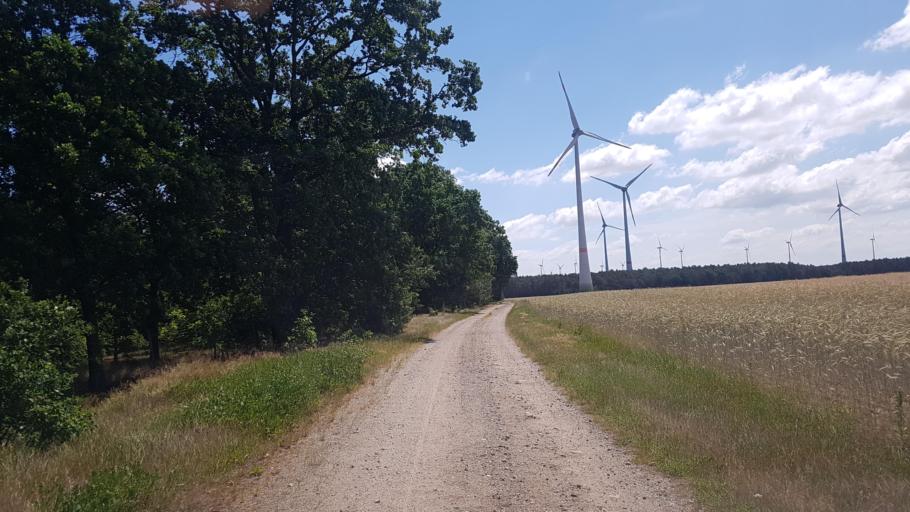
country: DE
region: Brandenburg
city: Treuenbrietzen
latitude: 52.0269
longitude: 12.8568
